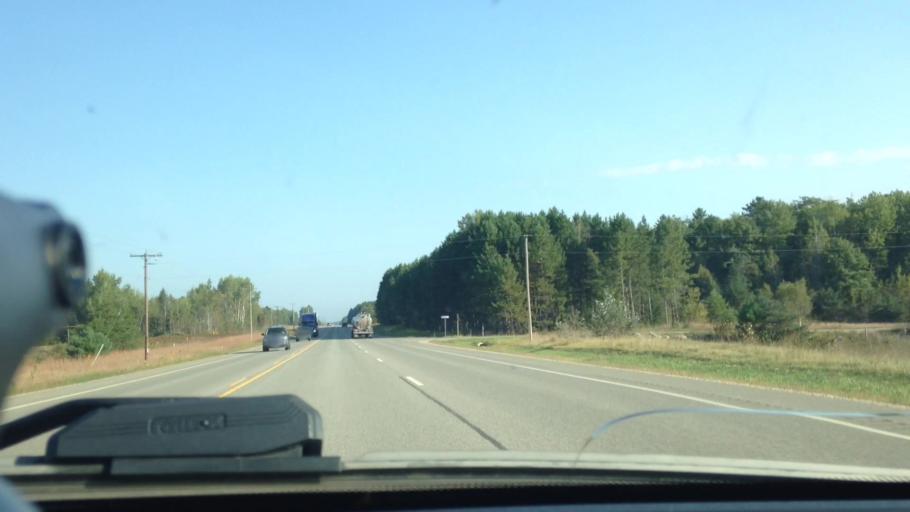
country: US
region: Wisconsin
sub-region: Marinette County
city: Niagara
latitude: 45.5346
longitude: -87.9970
